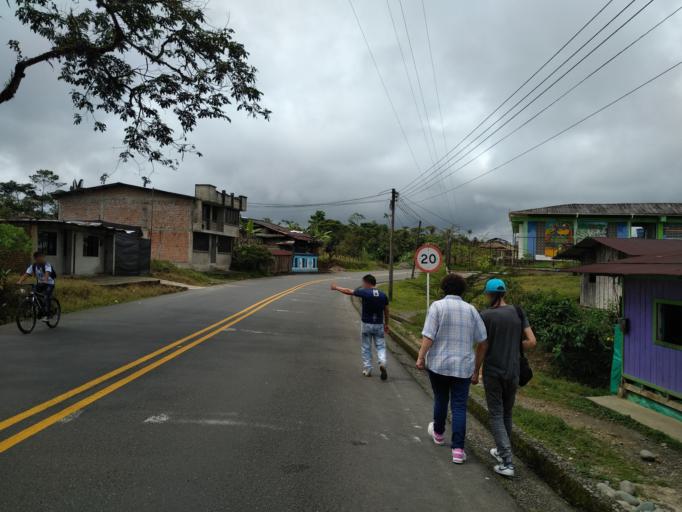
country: CO
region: Narino
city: Ricaurte
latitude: 1.3623
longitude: -78.1820
